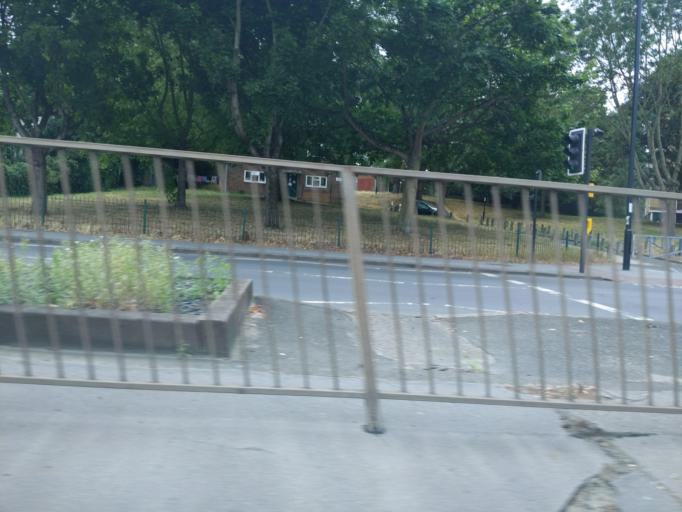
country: GB
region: England
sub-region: Greater London
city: South Croydon
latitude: 51.3700
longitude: -0.1055
